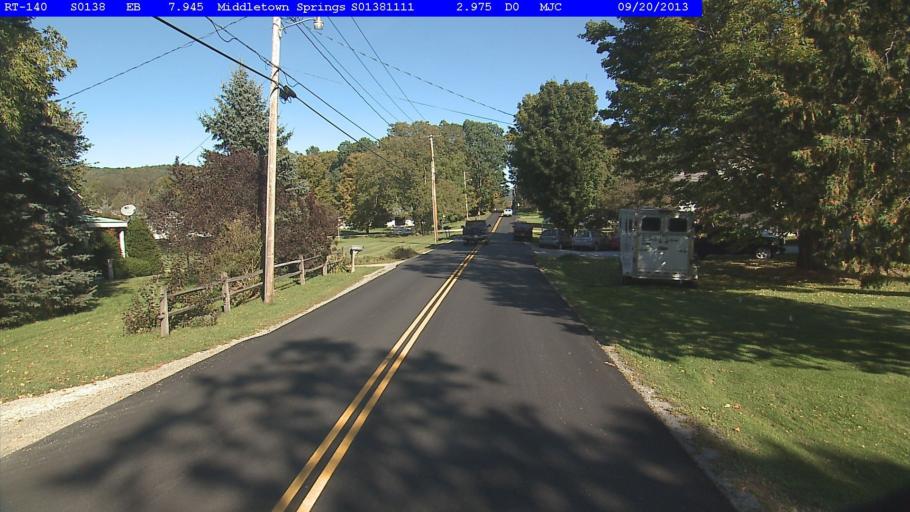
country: US
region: Vermont
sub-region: Rutland County
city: Poultney
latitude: 43.4853
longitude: -73.1228
